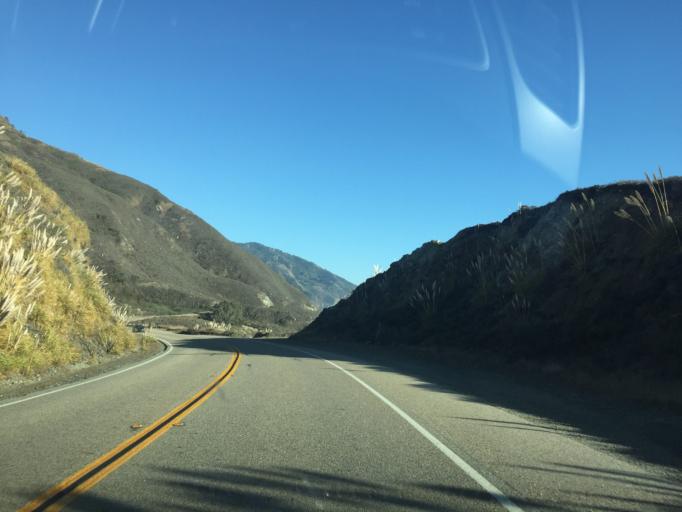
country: US
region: California
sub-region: Monterey County
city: King City
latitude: 35.8720
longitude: -121.4437
